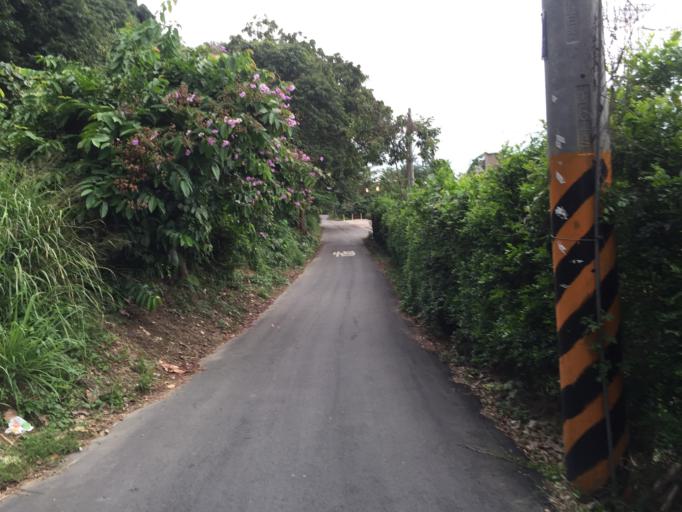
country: TW
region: Taiwan
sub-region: Taichung City
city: Taichung
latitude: 24.0703
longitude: 120.7076
